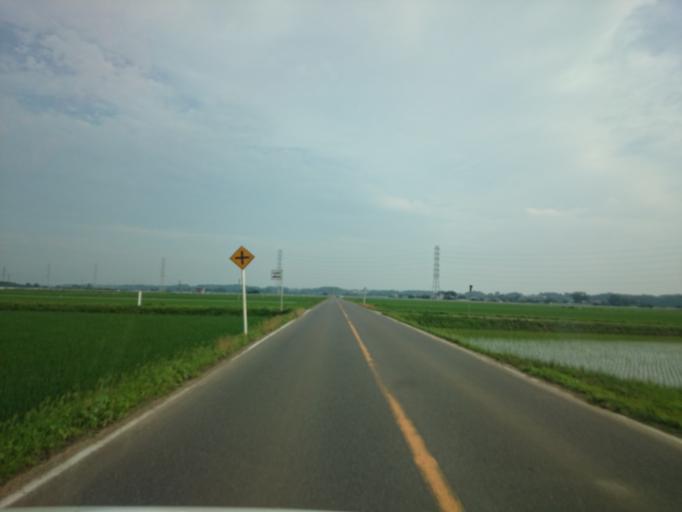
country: JP
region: Ibaraki
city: Tsukuba
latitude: 36.1582
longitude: 140.0992
